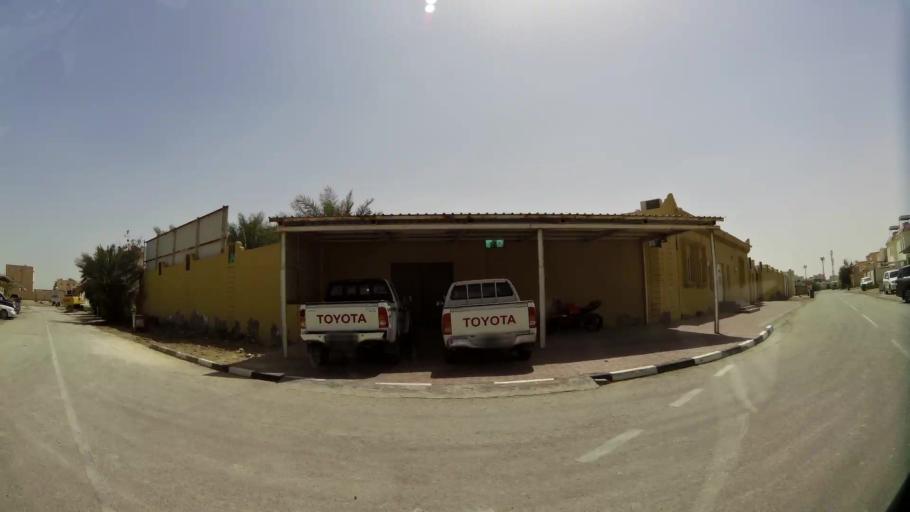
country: QA
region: Baladiyat Umm Salal
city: Umm Salal Muhammad
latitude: 25.3809
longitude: 51.4262
